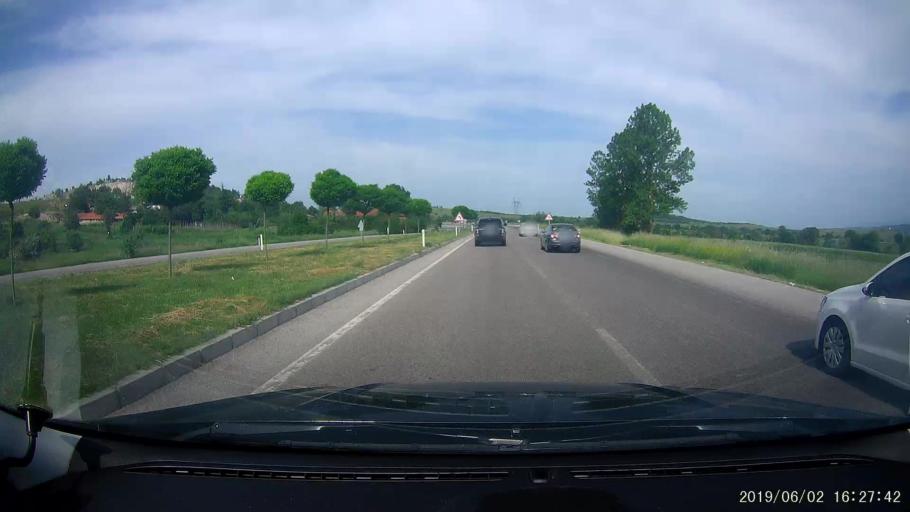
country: TR
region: Samsun
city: Ladik
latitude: 41.0018
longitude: 35.8324
